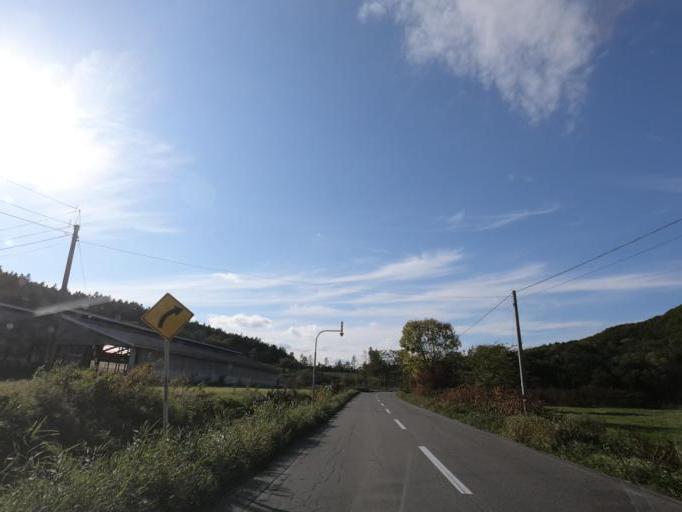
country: JP
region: Hokkaido
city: Obihiro
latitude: 42.6171
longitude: 143.4114
